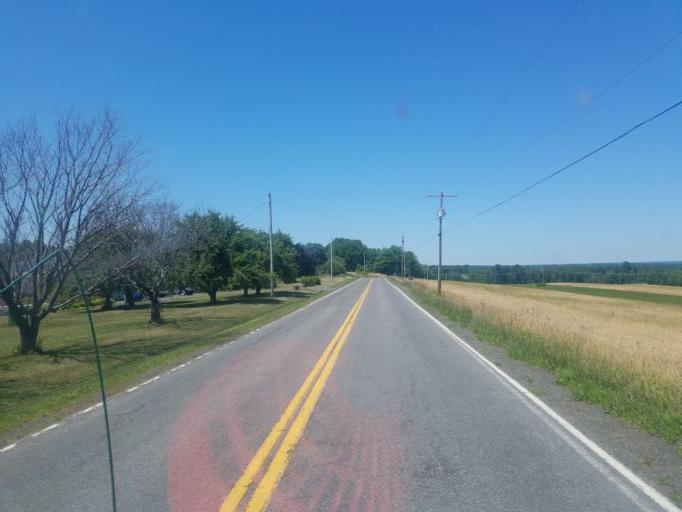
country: US
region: New York
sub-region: Yates County
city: Penn Yan
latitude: 42.7479
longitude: -77.0026
